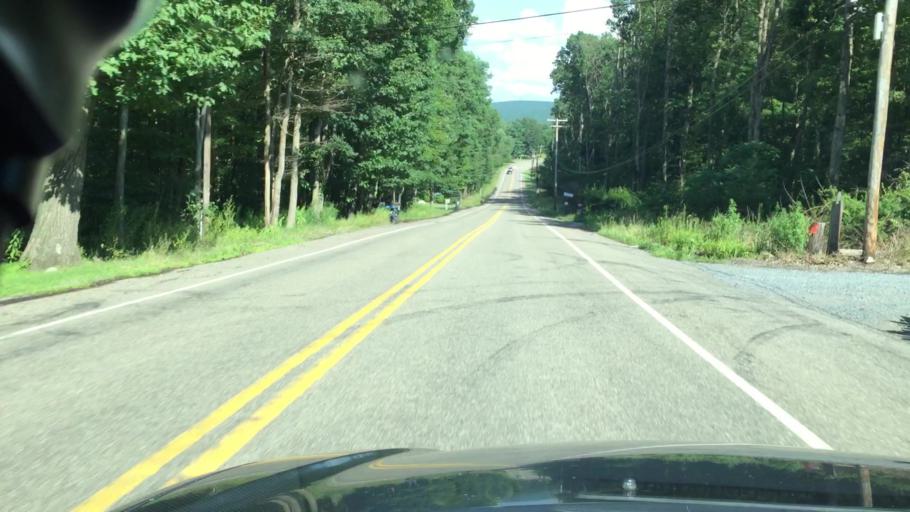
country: US
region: Pennsylvania
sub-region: Carbon County
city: Weatherly
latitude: 40.9271
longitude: -75.8731
